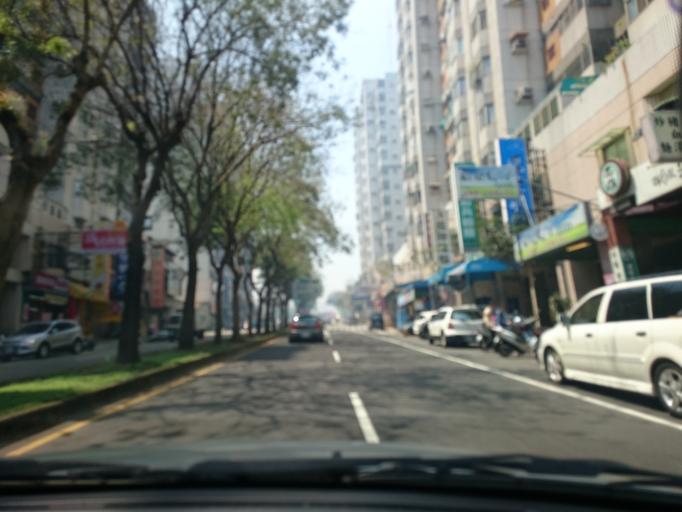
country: TW
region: Taiwan
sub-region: Taichung City
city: Taichung
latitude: 24.1874
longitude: 120.6069
